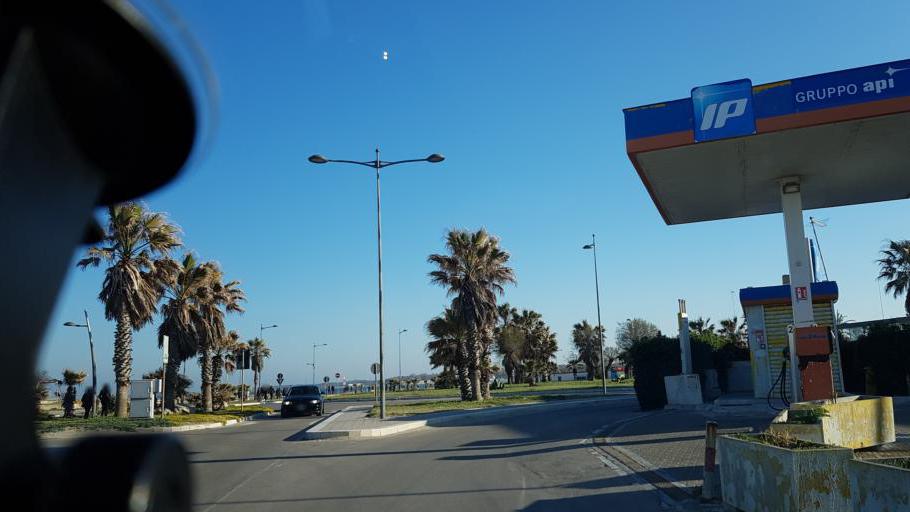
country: IT
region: Apulia
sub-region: Provincia di Lecce
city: Struda
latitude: 40.3905
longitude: 18.3055
